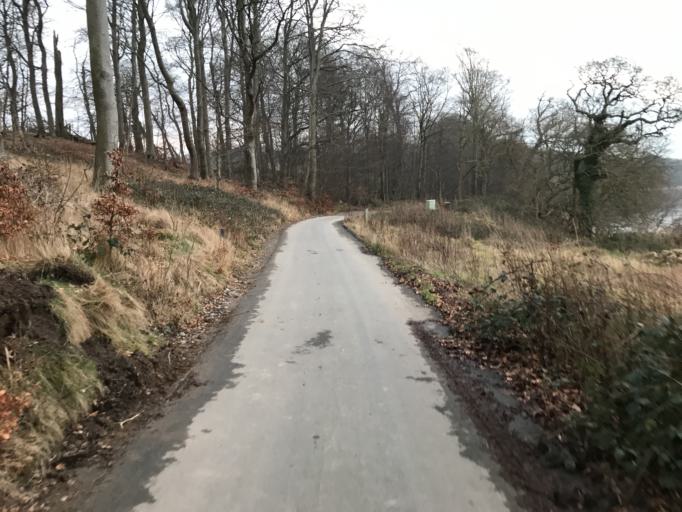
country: DK
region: South Denmark
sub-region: Fredericia Kommune
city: Snoghoj
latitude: 55.5026
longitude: 9.6929
